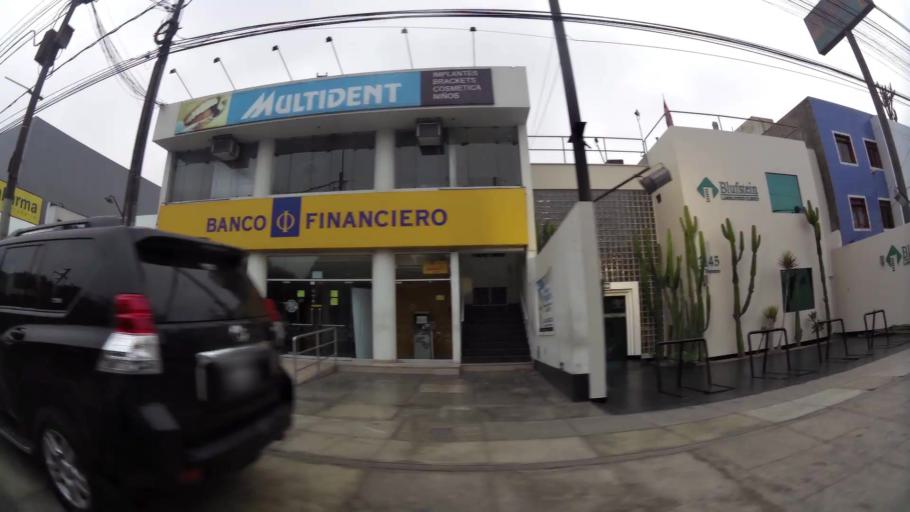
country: PE
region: Lima
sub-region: Lima
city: La Molina
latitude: -12.0900
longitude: -76.9491
